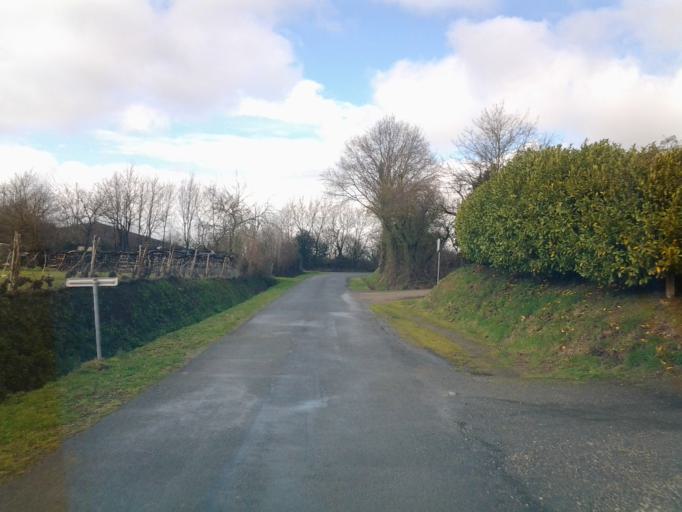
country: FR
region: Pays de la Loire
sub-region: Departement de la Vendee
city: Nesmy
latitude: 46.6469
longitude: -1.3635
